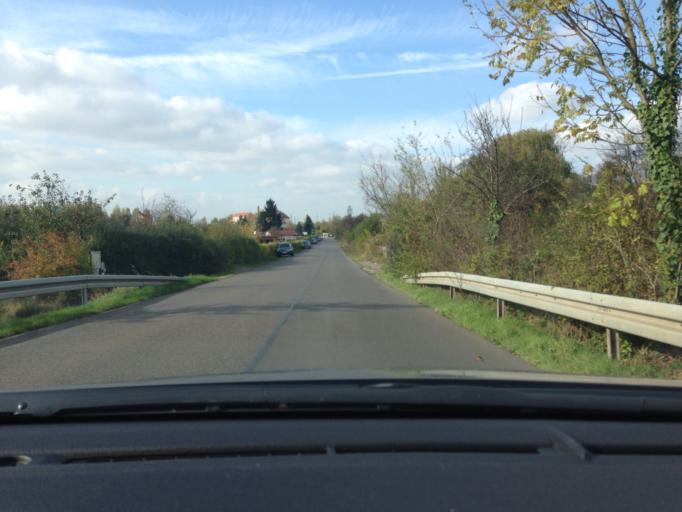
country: DE
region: Saxony
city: Taucha
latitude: 51.3406
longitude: 12.4553
